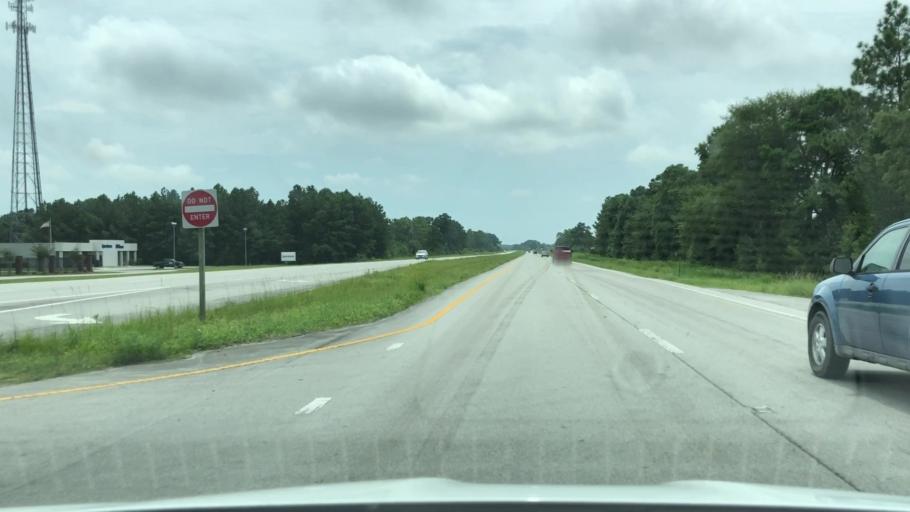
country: US
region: North Carolina
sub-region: Carteret County
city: Newport
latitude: 34.8022
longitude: -76.8786
